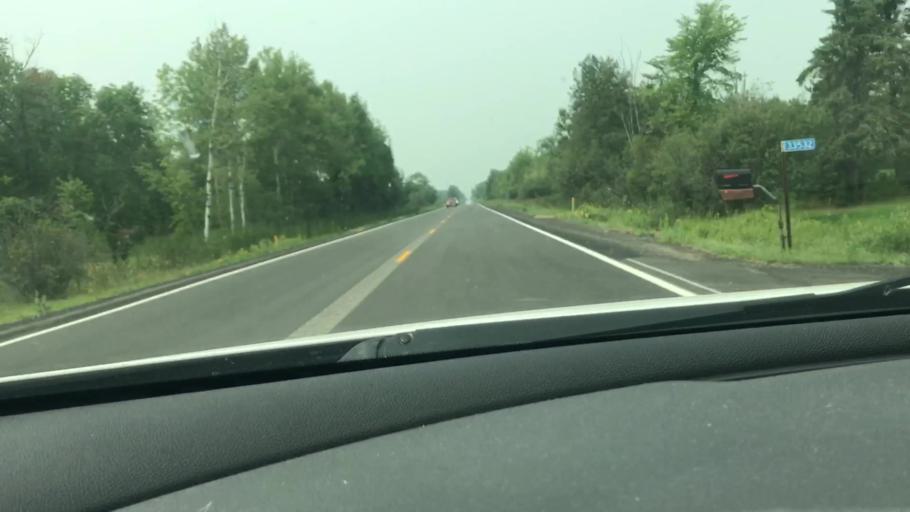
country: US
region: Minnesota
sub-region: Itasca County
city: Cohasset
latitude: 47.3616
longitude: -93.8654
